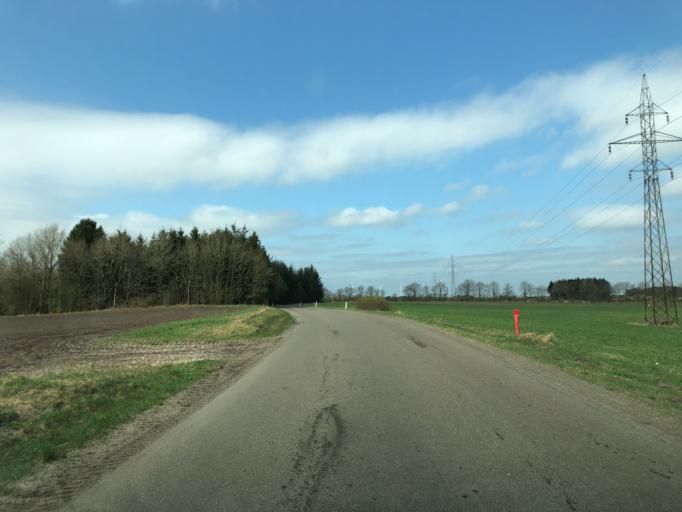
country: DK
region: South Denmark
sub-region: Vejle Kommune
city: Give
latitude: 55.9154
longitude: 9.2222
